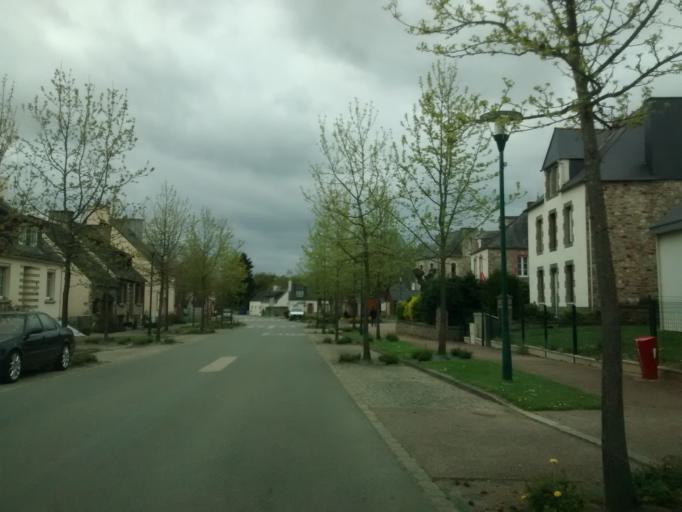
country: FR
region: Brittany
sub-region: Departement du Morbihan
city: Malestroit
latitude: 47.8038
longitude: -2.4173
